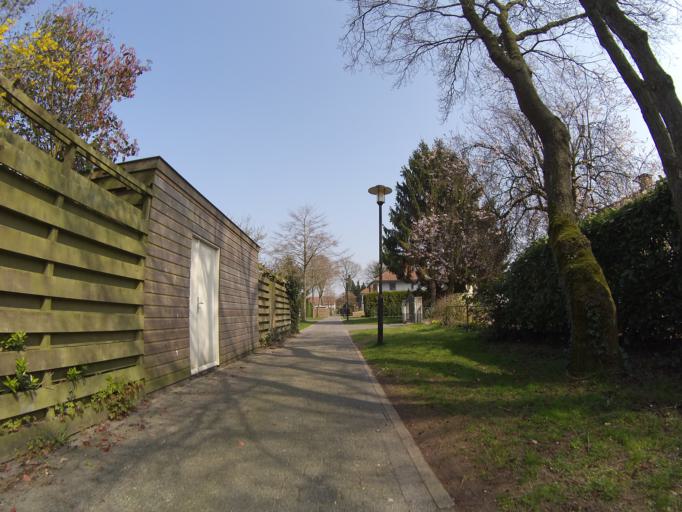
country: NL
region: Utrecht
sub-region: Gemeente Amersfoort
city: Hoogland
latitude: 52.1904
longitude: 5.4024
